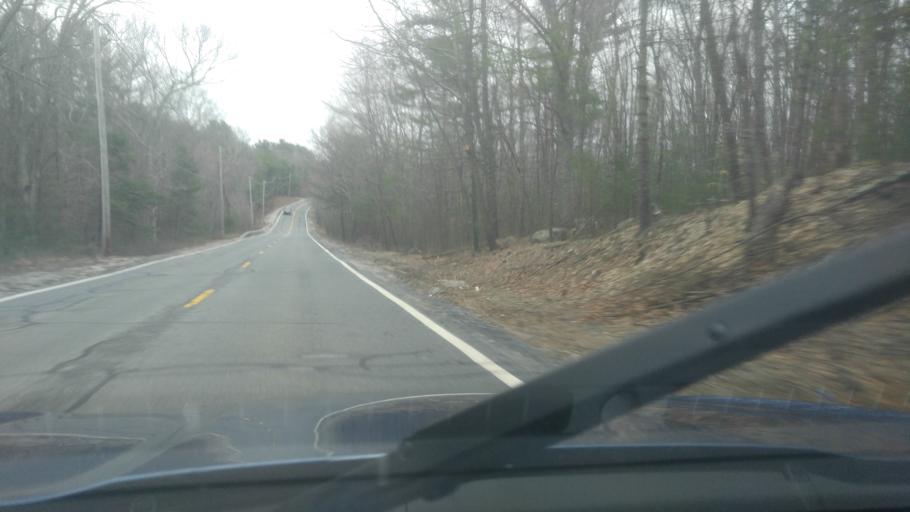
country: US
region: Rhode Island
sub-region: Kent County
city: West Greenwich
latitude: 41.6742
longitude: -71.6420
